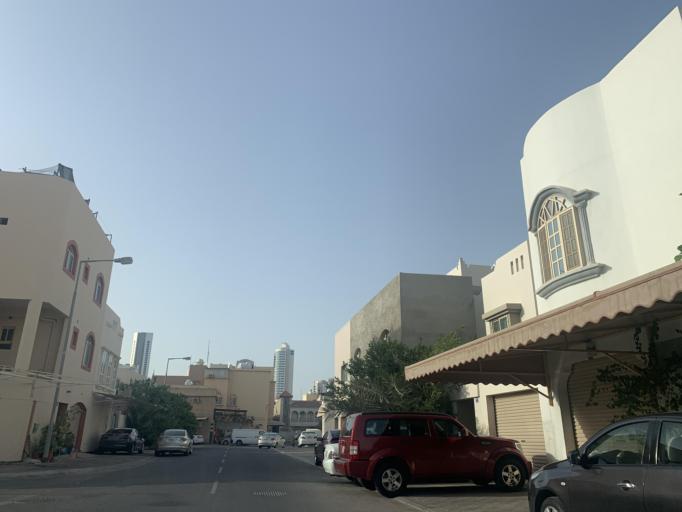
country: BH
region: Manama
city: Jidd Hafs
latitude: 26.2226
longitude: 50.5493
